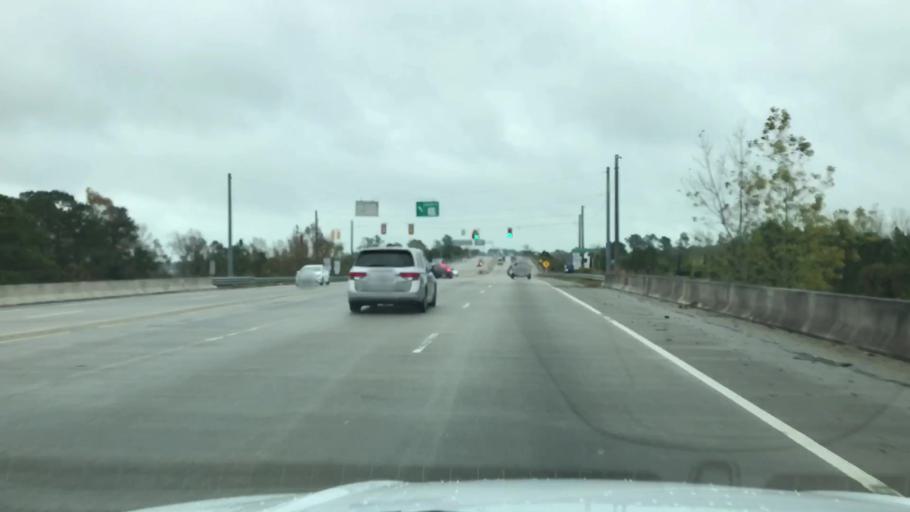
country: US
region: South Carolina
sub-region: Horry County
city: Myrtle Beach
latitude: 33.7541
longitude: -78.8527
